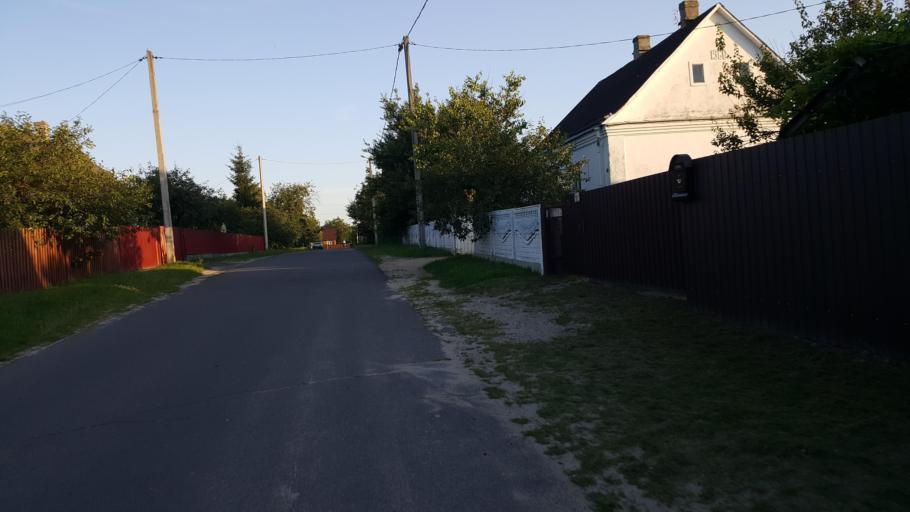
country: BY
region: Brest
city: Kamyanyets
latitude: 52.3981
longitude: 23.8207
